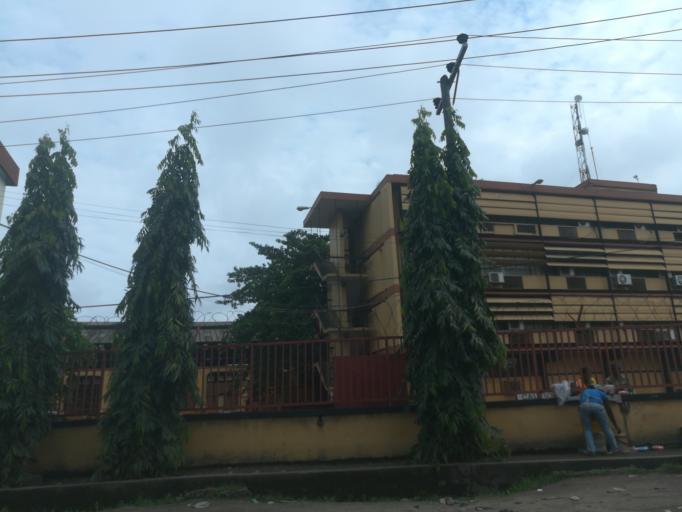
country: NG
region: Lagos
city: Agege
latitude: 6.6142
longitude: 3.3351
